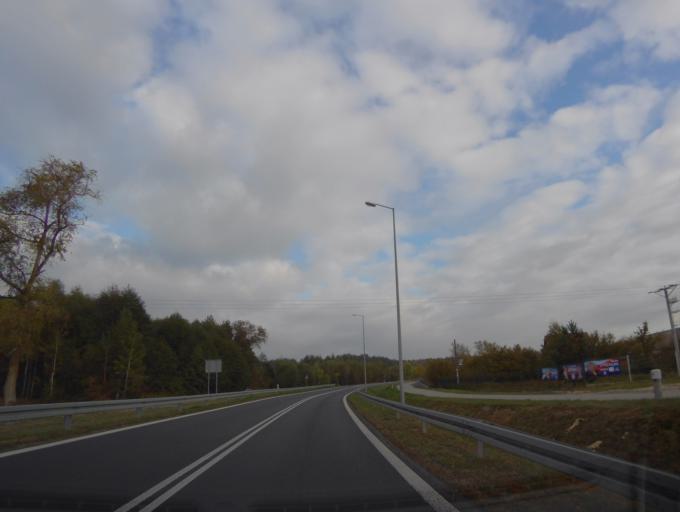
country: PL
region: Lublin Voivodeship
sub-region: Powiat bilgorajski
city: Frampol
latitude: 50.6116
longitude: 22.6730
